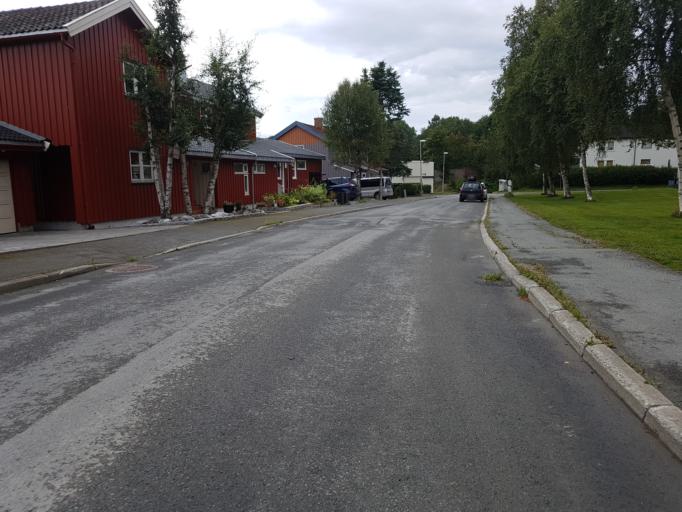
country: NO
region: Sor-Trondelag
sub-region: Trondheim
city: Trondheim
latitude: 63.4034
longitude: 10.4148
